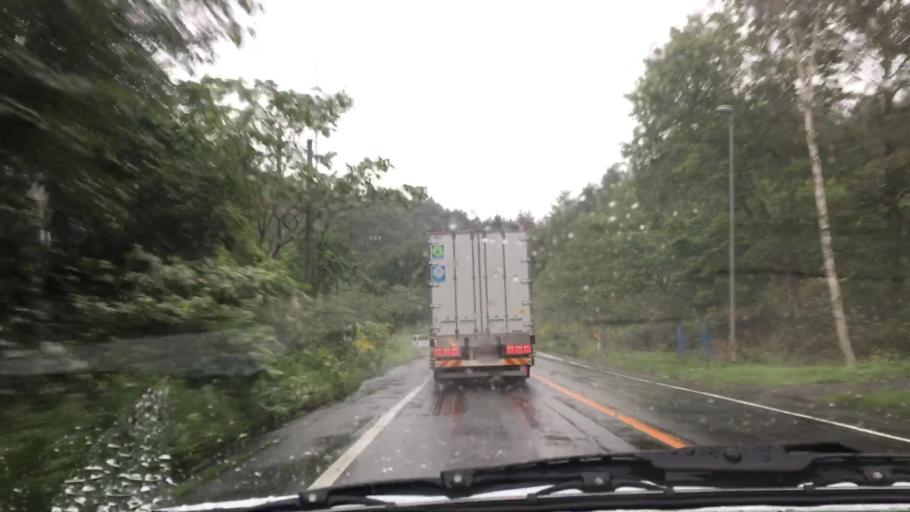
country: JP
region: Hokkaido
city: Niseko Town
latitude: 42.5963
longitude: 140.6737
